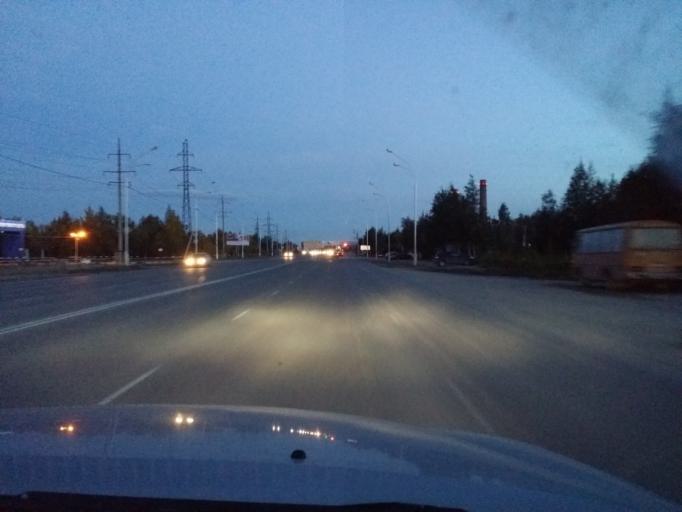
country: RU
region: Khanty-Mansiyskiy Avtonomnyy Okrug
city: Nizhnevartovsk
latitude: 60.9519
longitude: 76.5298
